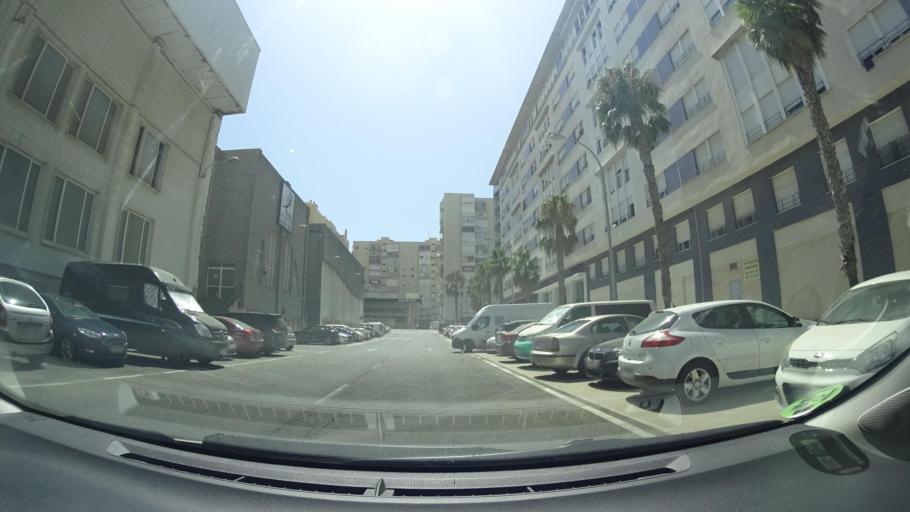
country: ES
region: Andalusia
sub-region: Provincia de Cadiz
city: Cadiz
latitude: 36.4986
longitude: -6.2712
